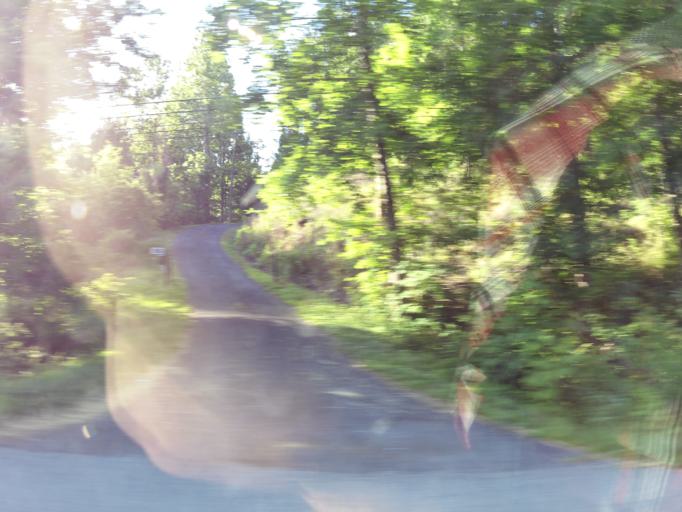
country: US
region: Tennessee
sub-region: Sevier County
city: Seymour
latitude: 35.8488
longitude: -83.7033
